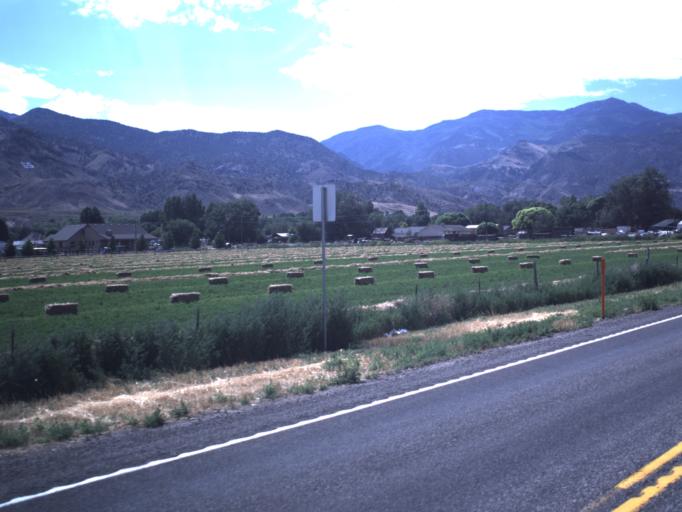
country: US
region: Utah
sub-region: Sevier County
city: Monroe
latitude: 38.6424
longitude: -112.1215
